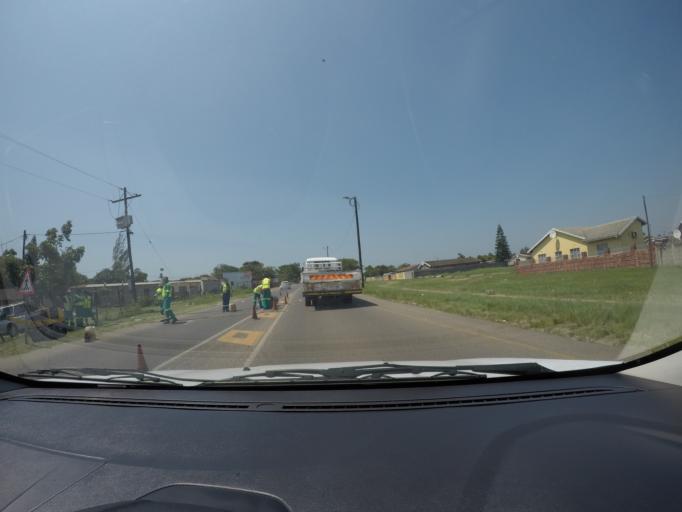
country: ZA
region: KwaZulu-Natal
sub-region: uThungulu District Municipality
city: eSikhawini
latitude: -28.8648
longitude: 31.9256
